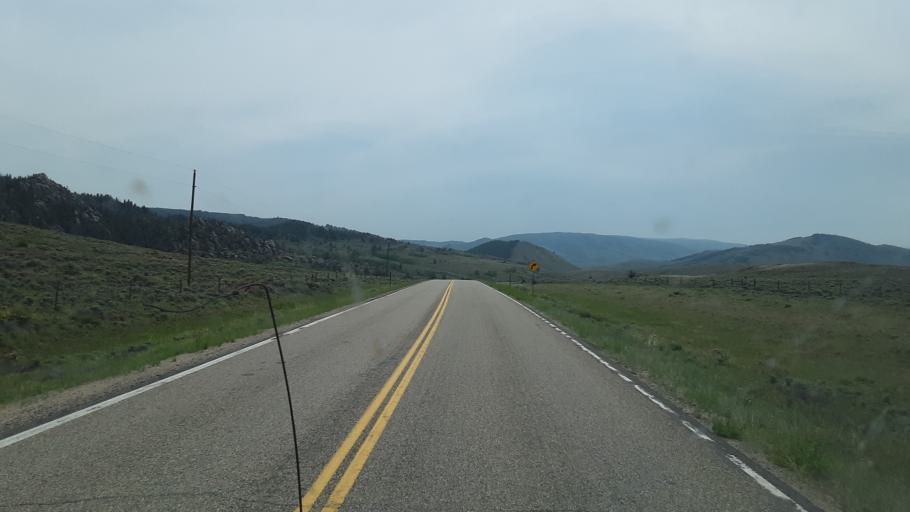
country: US
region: Colorado
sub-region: Jackson County
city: Walden
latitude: 40.9243
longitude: -106.3215
